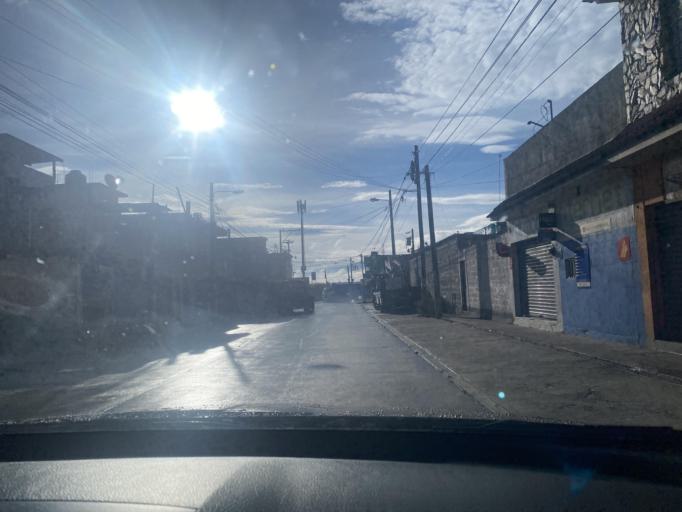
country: GT
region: Quetzaltenango
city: Olintepeque
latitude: 14.8654
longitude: -91.5136
